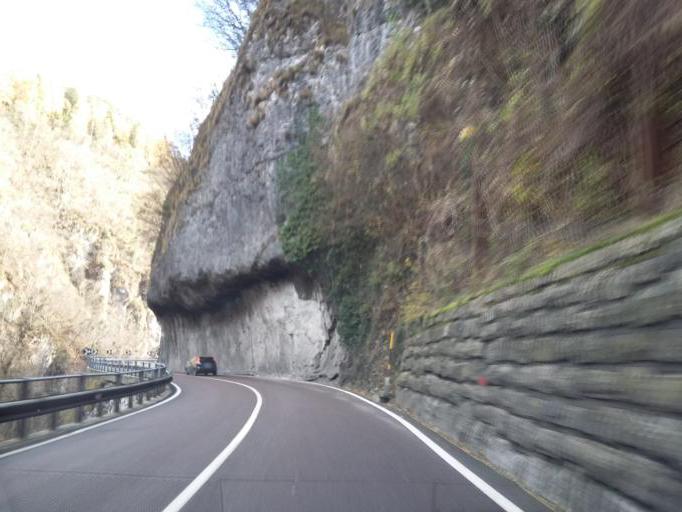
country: IT
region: Trentino-Alto Adige
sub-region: Provincia di Trento
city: Stenico
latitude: 46.0481
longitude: 10.8467
